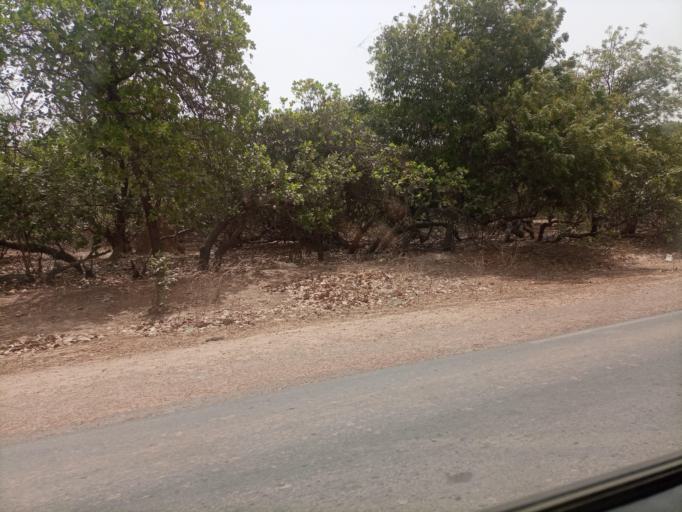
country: SN
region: Fatick
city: Sokone
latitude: 13.7092
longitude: -16.4282
